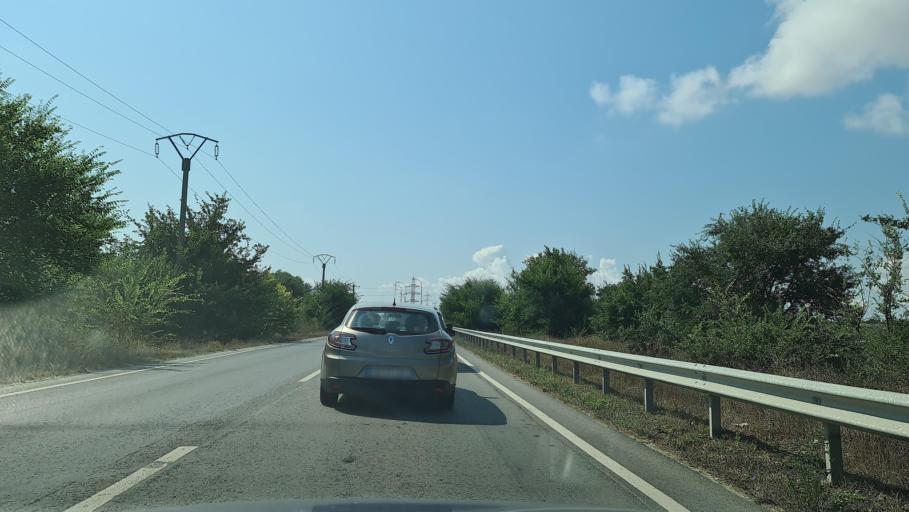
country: RO
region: Constanta
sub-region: Comuna Agigea
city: Agigea
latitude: 44.0886
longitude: 28.6401
